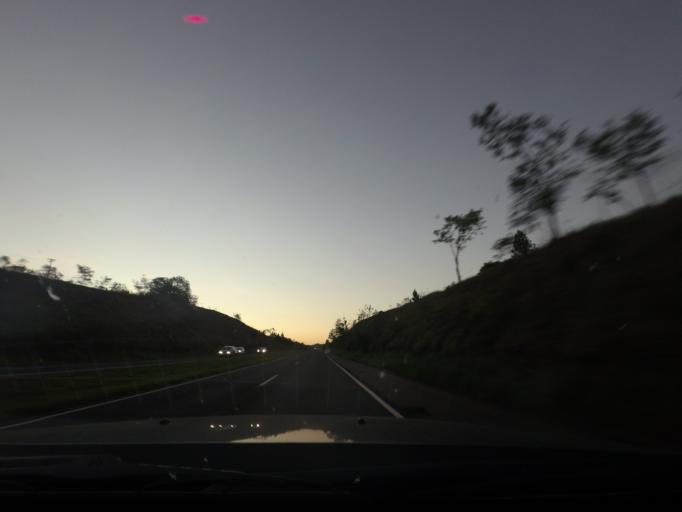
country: BR
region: Sao Paulo
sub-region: Piracicaba
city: Piracicaba
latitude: -22.7365
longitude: -47.5311
